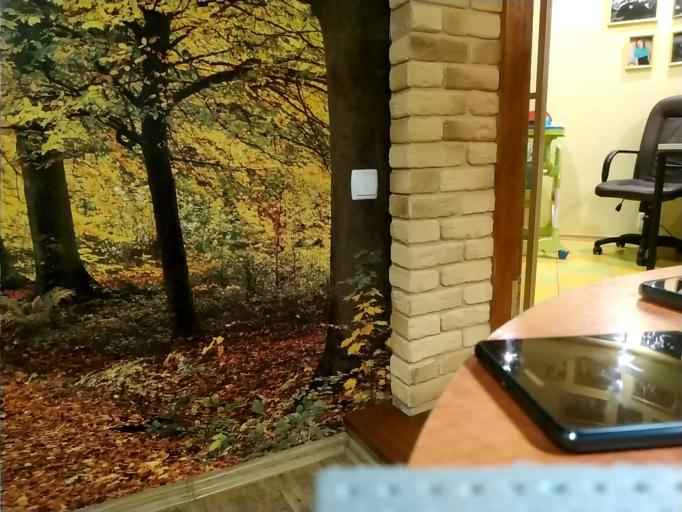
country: RU
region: Tverskaya
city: Zubtsov
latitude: 56.2245
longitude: 34.7093
